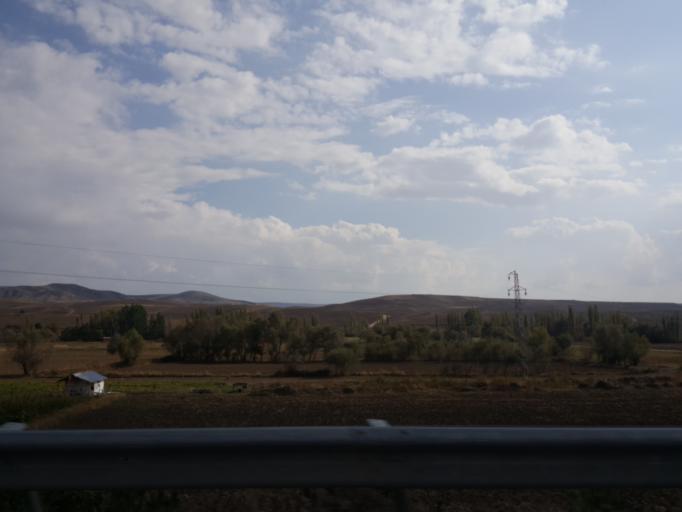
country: TR
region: Corum
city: Sungurlu
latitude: 40.2103
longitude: 34.5457
